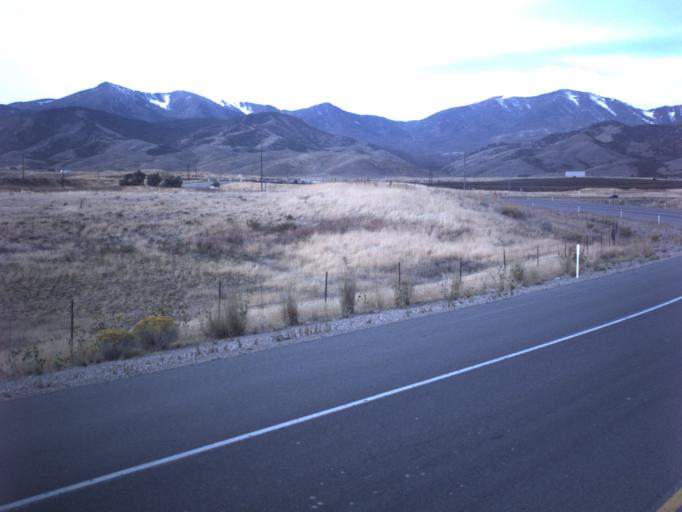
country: US
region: Utah
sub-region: Salt Lake County
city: Oquirrh
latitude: 40.6547
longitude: -112.0720
